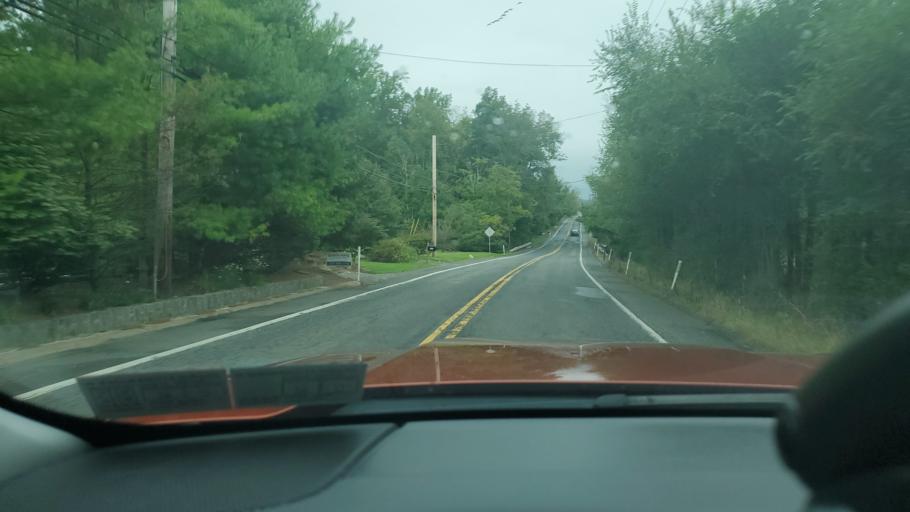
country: US
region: Pennsylvania
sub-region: Montgomery County
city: Woxall
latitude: 40.3066
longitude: -75.4806
